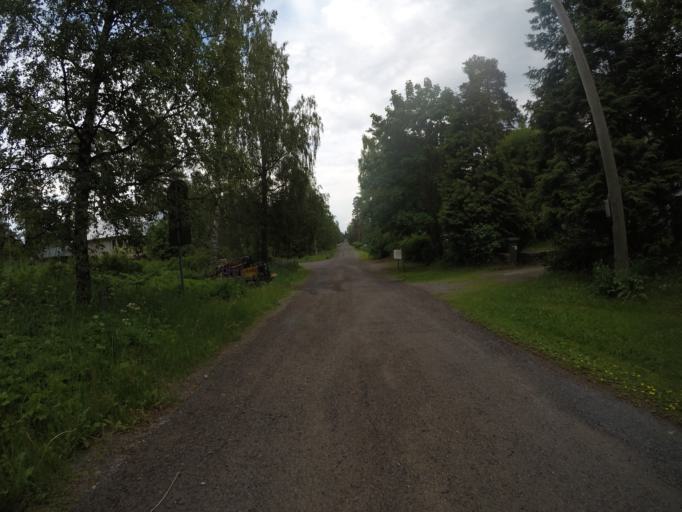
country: FI
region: Haeme
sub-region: Haemeenlinna
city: Haemeenlinna
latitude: 61.0132
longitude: 24.4877
